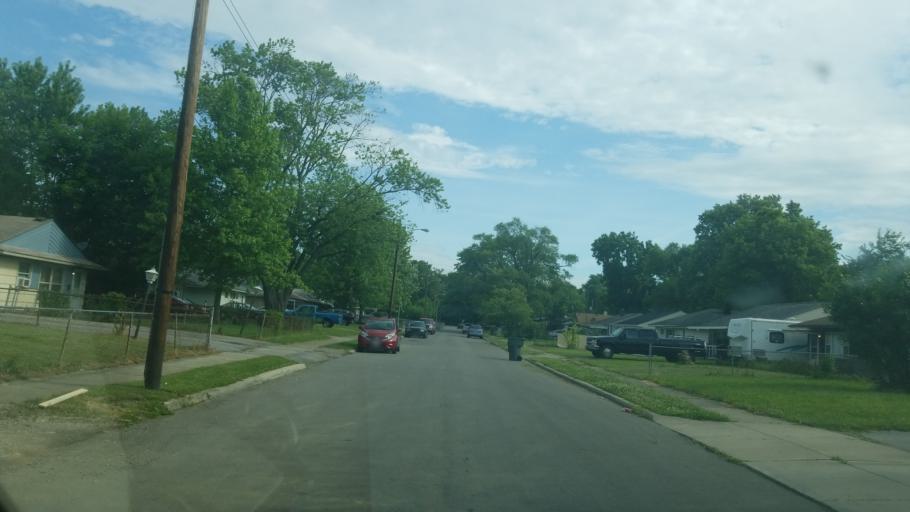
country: US
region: Ohio
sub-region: Franklin County
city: Minerva Park
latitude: 40.0386
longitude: -82.9735
